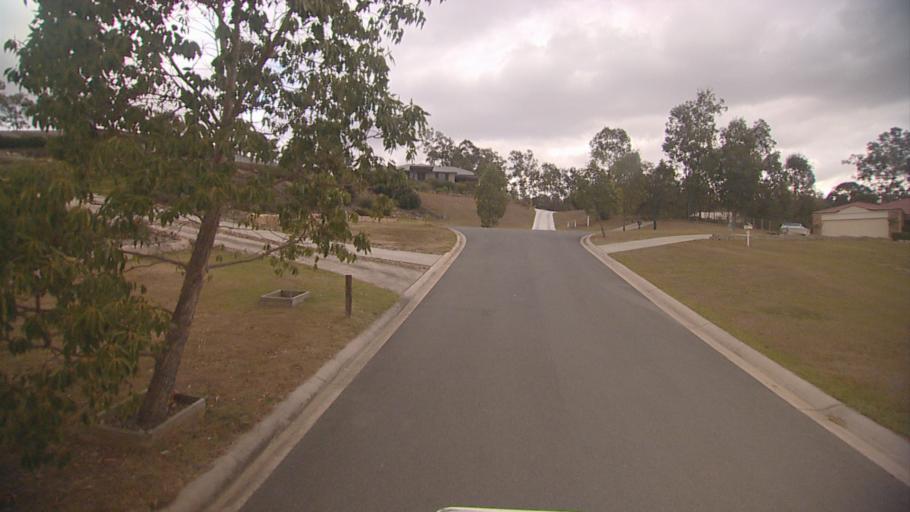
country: AU
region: Queensland
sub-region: Logan
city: Cedar Vale
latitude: -27.8659
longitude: 153.0792
